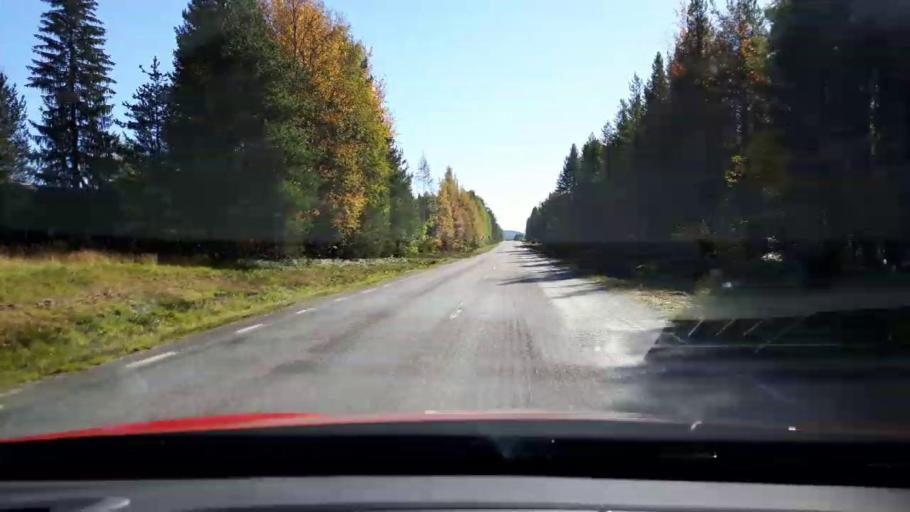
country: SE
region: Jaemtland
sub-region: Harjedalens Kommun
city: Sveg
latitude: 62.3084
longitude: 14.0443
